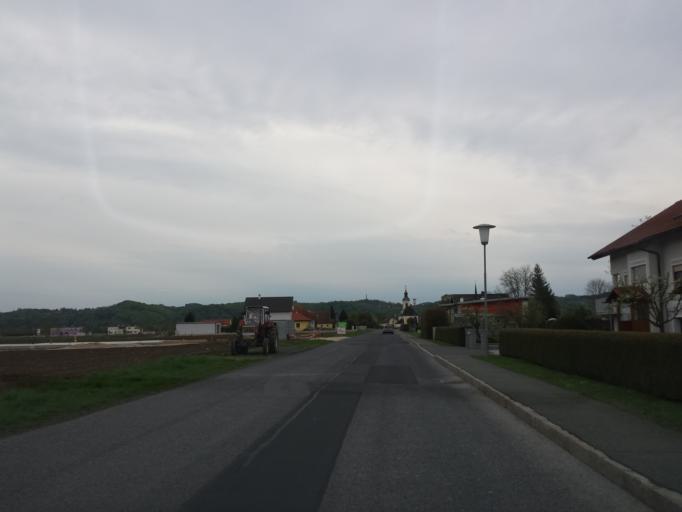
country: AT
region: Burgenland
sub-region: Politischer Bezirk Jennersdorf
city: Konigsdorf
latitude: 47.0089
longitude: 16.1744
